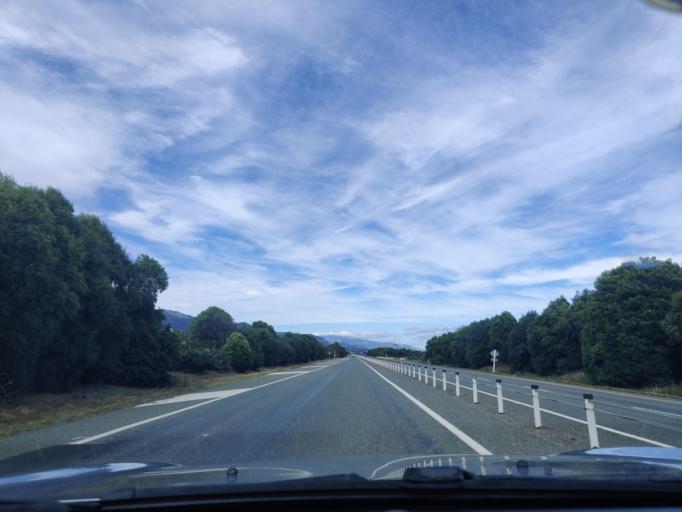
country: NZ
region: Tasman
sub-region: Tasman District
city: Richmond
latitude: -41.3106
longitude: 173.2183
